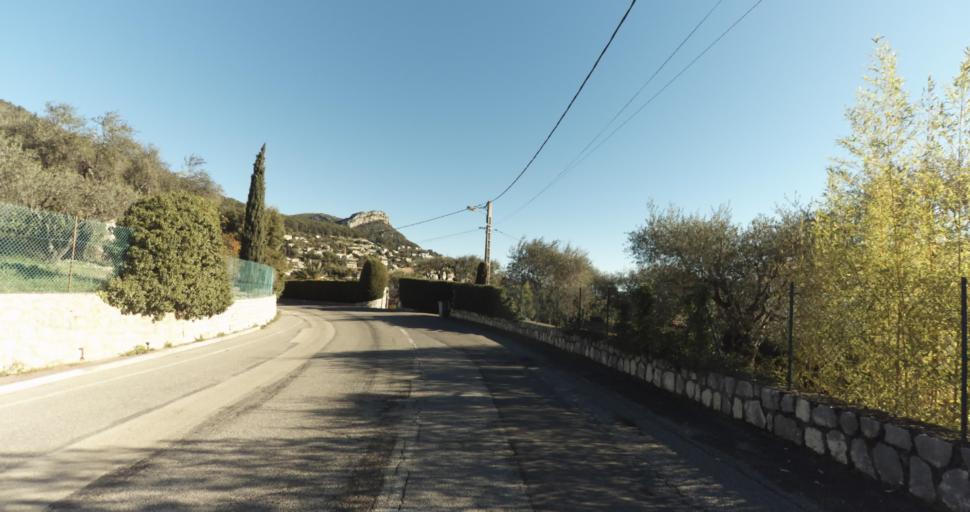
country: FR
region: Provence-Alpes-Cote d'Azur
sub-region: Departement des Alpes-Maritimes
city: Vence
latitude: 43.7244
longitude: 7.0863
